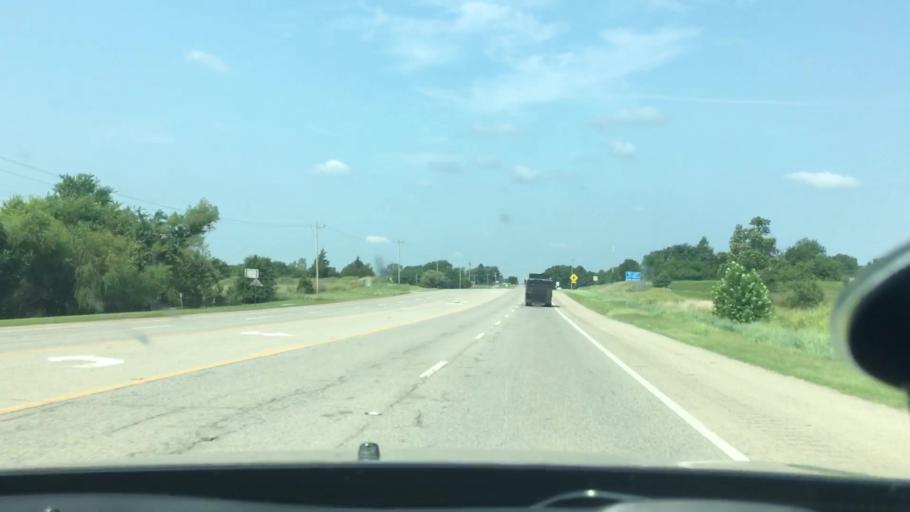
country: US
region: Oklahoma
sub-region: Bryan County
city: Calera
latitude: 33.9983
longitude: -96.4960
